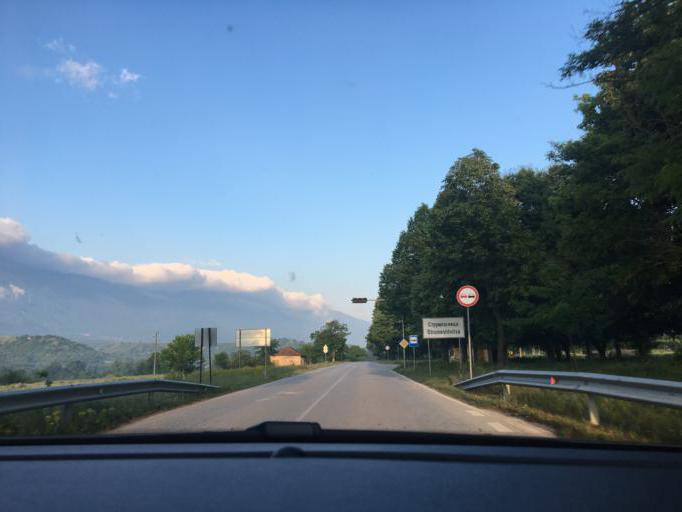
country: MK
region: Novo Selo
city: Novo Selo
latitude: 41.3955
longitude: 23.0477
